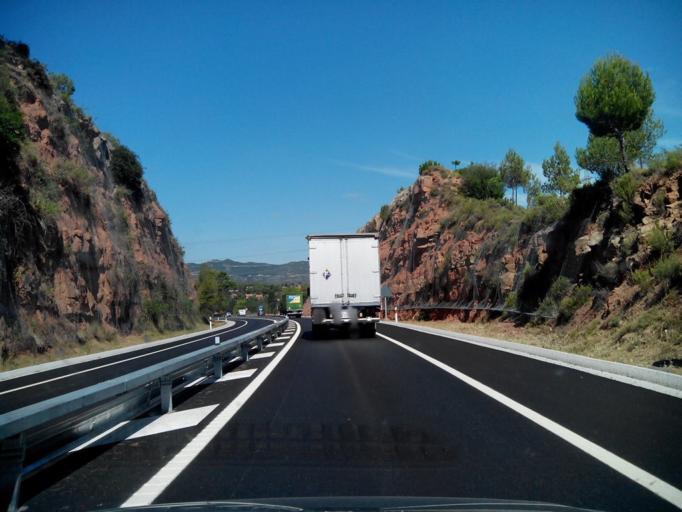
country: ES
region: Catalonia
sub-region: Provincia de Barcelona
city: Monistrol de Montserrat
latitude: 41.6020
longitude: 1.8890
